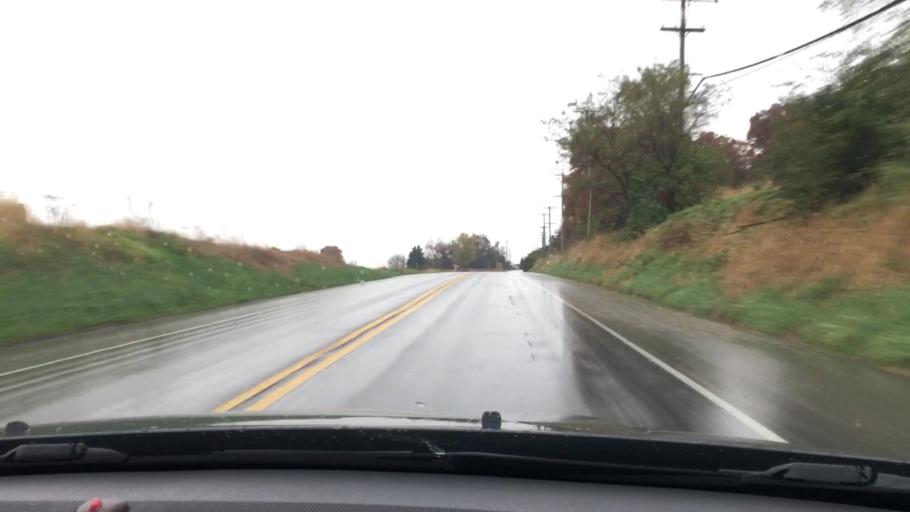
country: US
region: Pennsylvania
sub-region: York County
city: Susquehanna Trails
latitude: 39.8009
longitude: -76.3666
